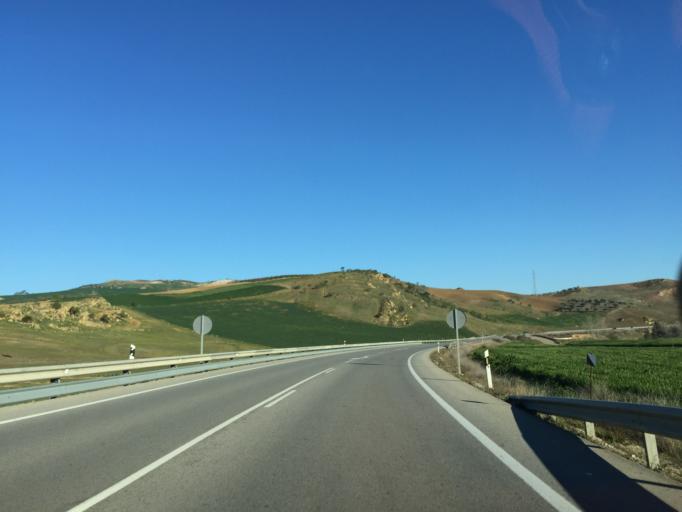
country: ES
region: Andalusia
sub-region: Provincia de Malaga
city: Ardales
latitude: 36.8902
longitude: -4.8475
